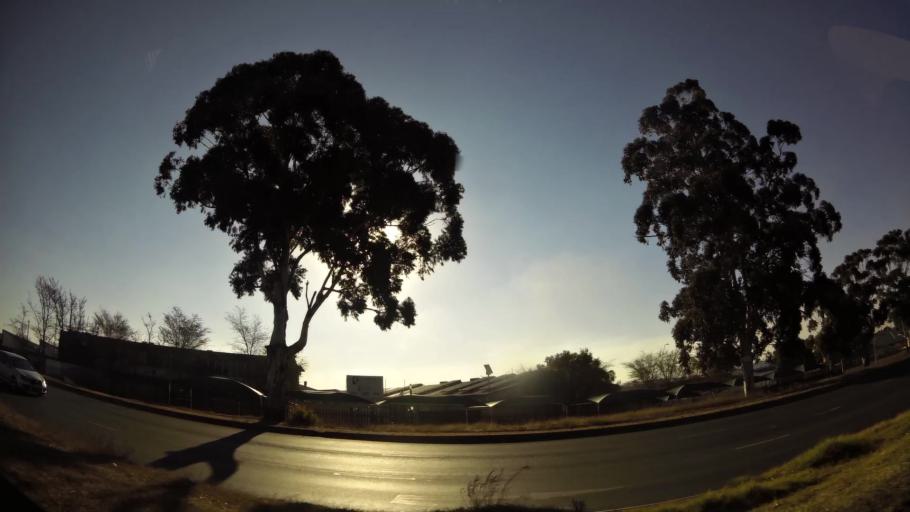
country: ZA
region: Gauteng
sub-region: City of Johannesburg Metropolitan Municipality
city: Johannesburg
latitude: -26.2023
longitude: 27.9669
